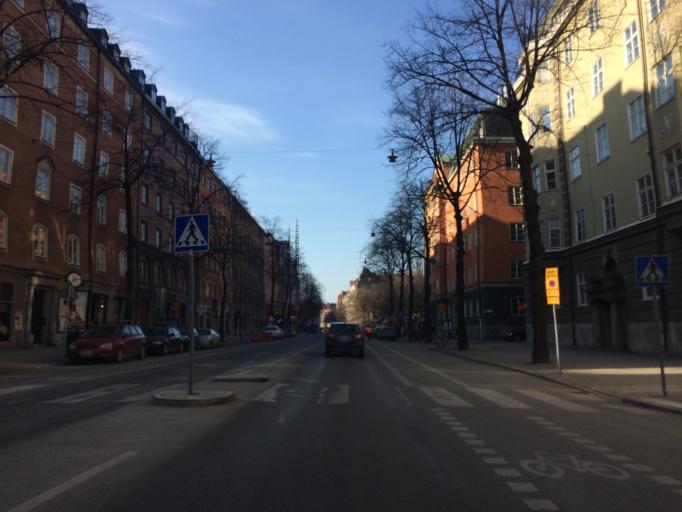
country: SE
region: Stockholm
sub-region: Stockholms Kommun
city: Stockholm
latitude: 59.3421
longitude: 18.0697
